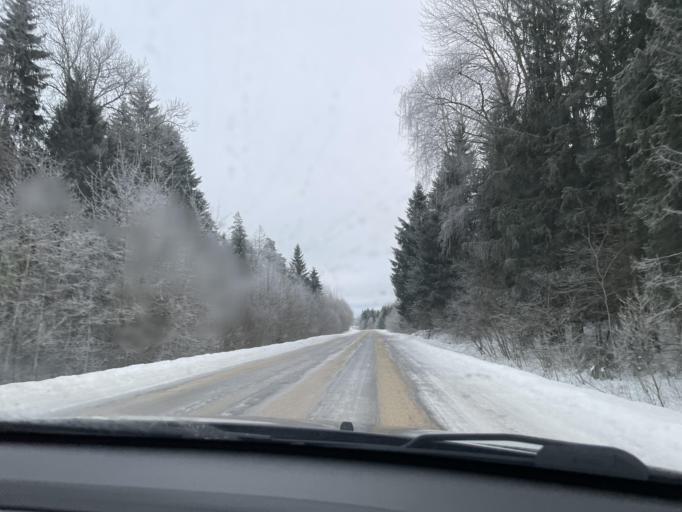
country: LV
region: Rezekne
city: Rezekne
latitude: 56.4993
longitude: 27.3871
